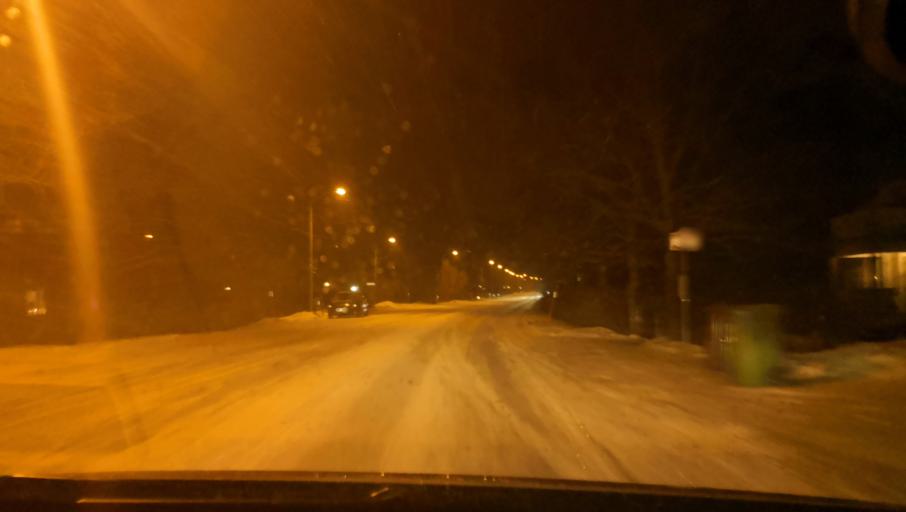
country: SE
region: Uppsala
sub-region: Heby Kommun
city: Tarnsjo
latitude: 60.1616
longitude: 16.9379
